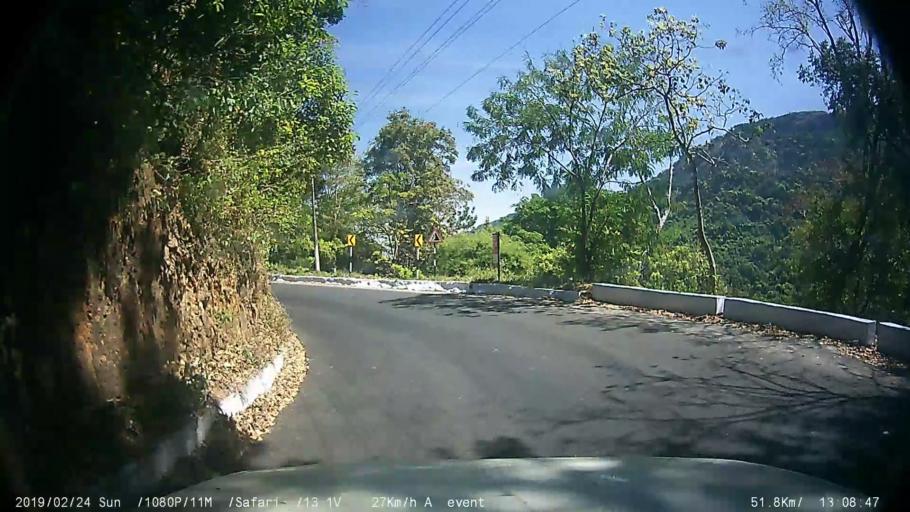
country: IN
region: Tamil Nadu
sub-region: Nilgiri
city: Wellington
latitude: 11.3385
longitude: 76.8386
